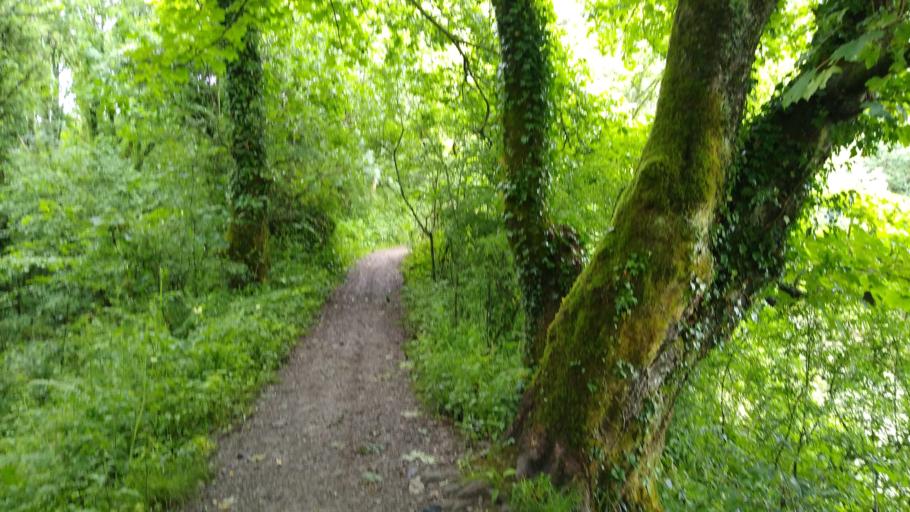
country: GB
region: England
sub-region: Cumbria
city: Maryport
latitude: 54.6875
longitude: -3.4879
